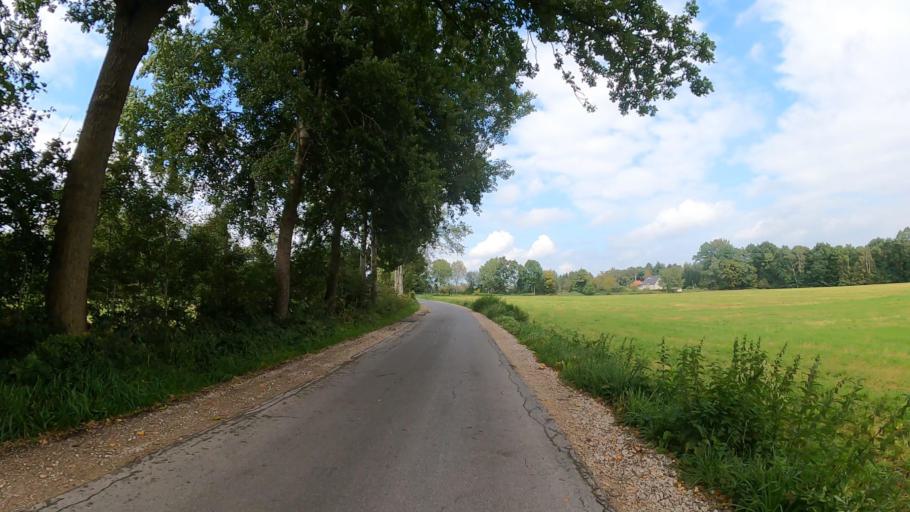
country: DE
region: Schleswig-Holstein
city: Tornesch
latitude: 53.7184
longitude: 9.7044
